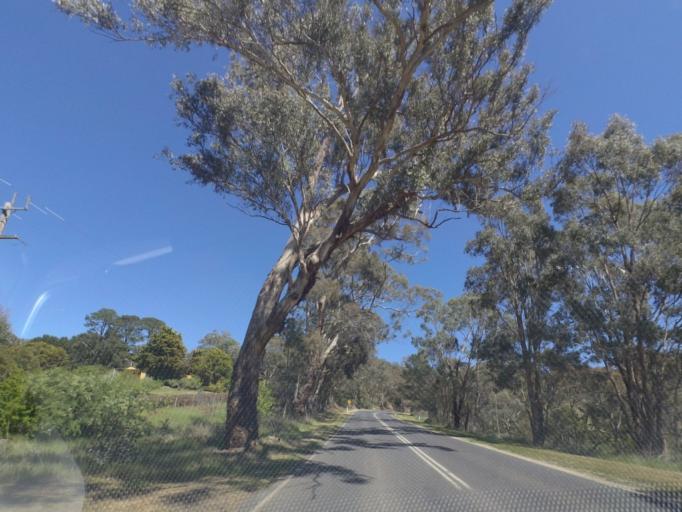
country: AU
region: Victoria
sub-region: Whittlesea
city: Whittlesea
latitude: -37.2884
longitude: 144.9753
